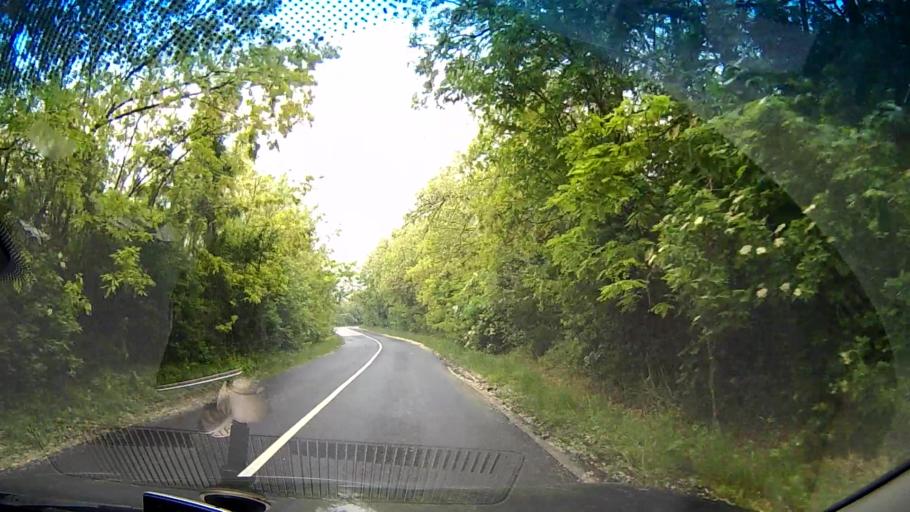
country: HU
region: Pest
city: Piliscsaba
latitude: 47.6371
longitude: 18.7837
